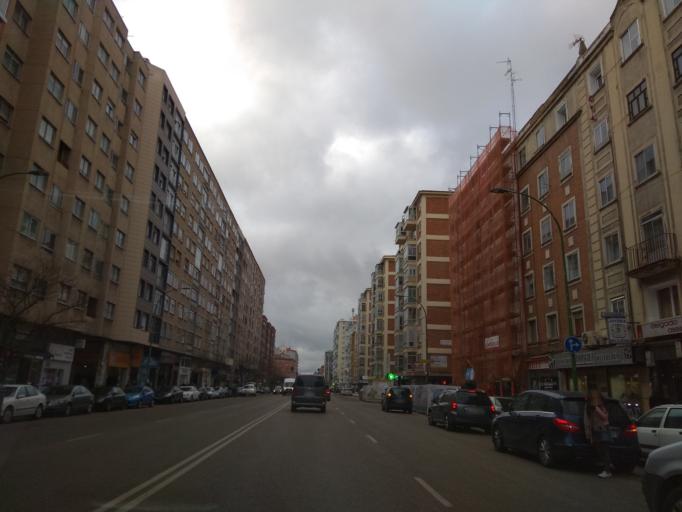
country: ES
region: Castille and Leon
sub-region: Provincia de Burgos
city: Burgos
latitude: 42.3519
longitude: -3.6717
